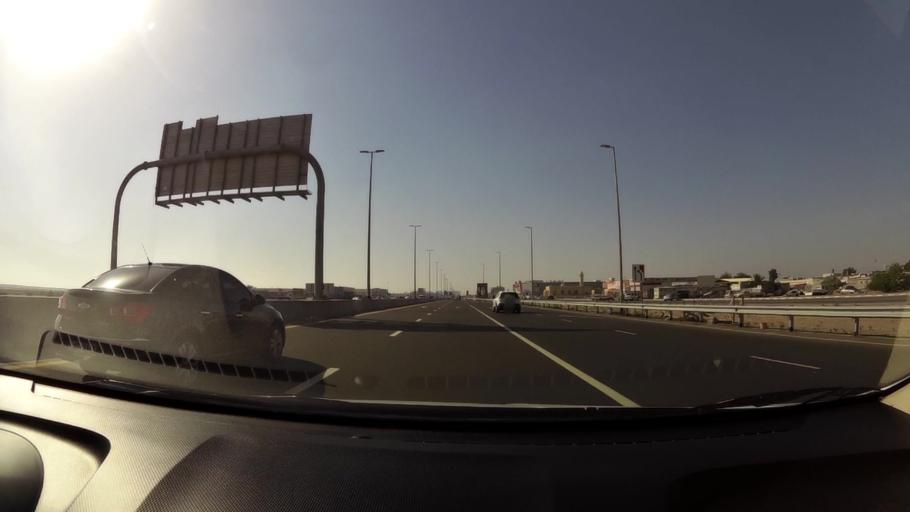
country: AE
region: Umm al Qaywayn
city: Umm al Qaywayn
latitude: 25.4991
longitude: 55.5511
